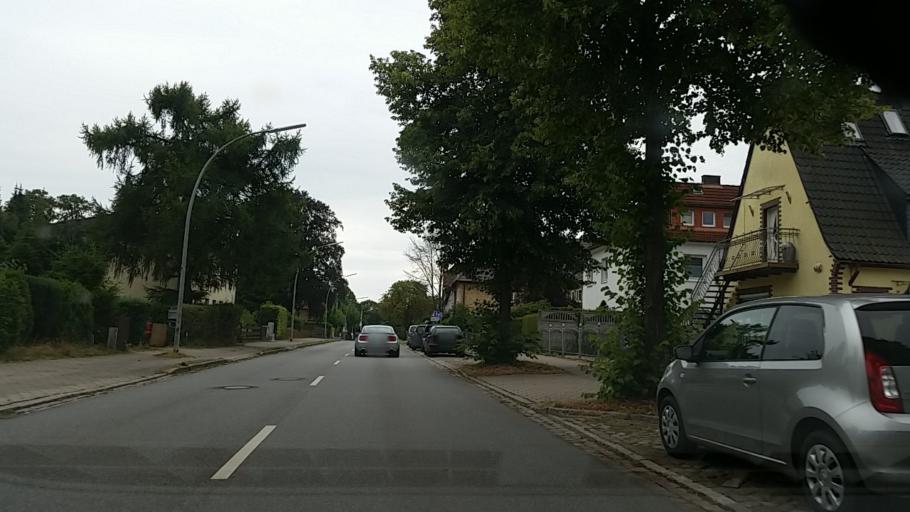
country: DE
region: Schleswig-Holstein
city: Reinbek
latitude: 53.5165
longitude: 10.2556
